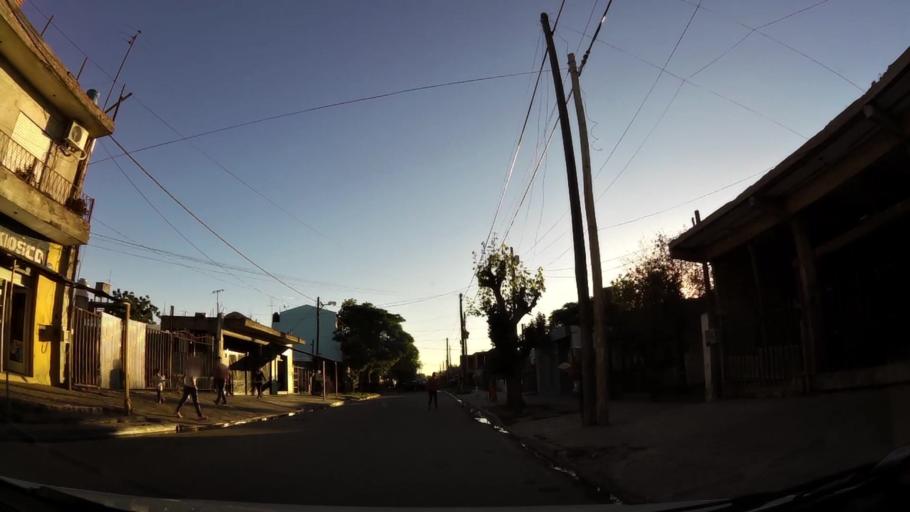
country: AR
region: Buenos Aires
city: San Justo
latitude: -34.7286
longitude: -58.6143
